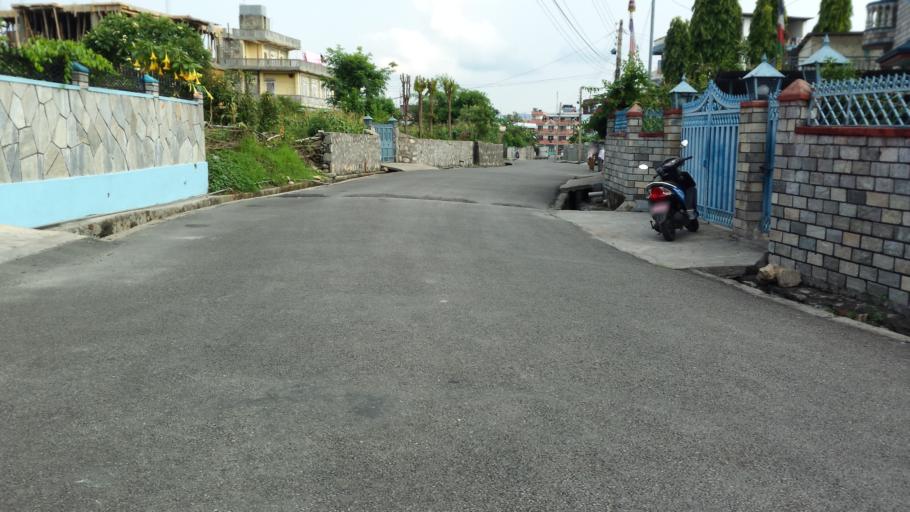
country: NP
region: Western Region
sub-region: Gandaki Zone
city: Pokhara
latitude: 28.2087
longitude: 83.9989
